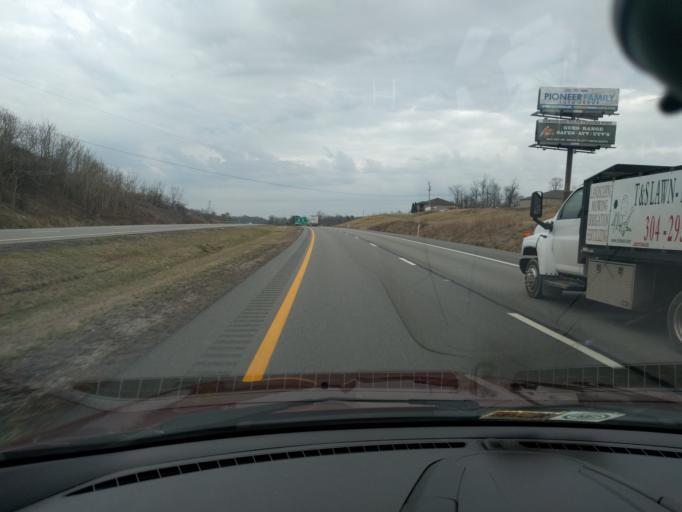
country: US
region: West Virginia
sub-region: Wood County
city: Boaz
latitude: 39.3068
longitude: -81.4840
